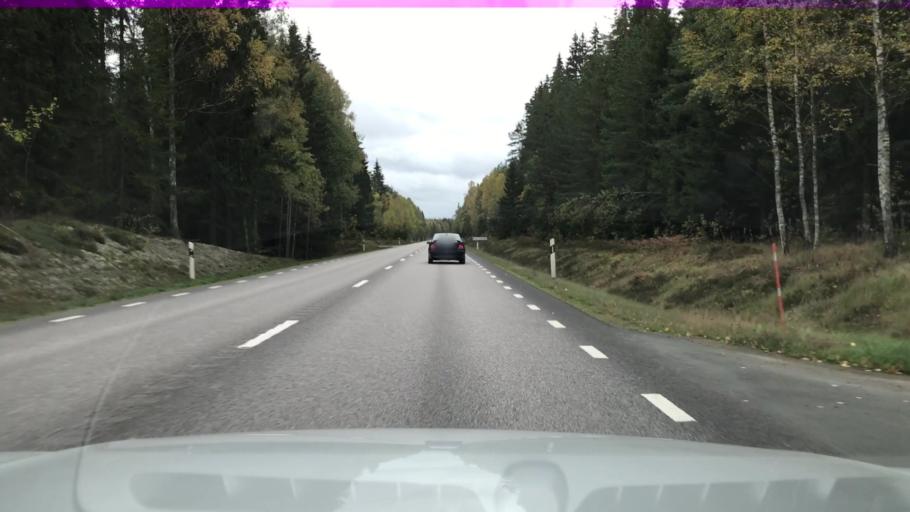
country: SE
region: Kalmar
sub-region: Hultsfreds Kommun
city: Hultsfred
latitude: 57.5483
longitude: 15.8455
